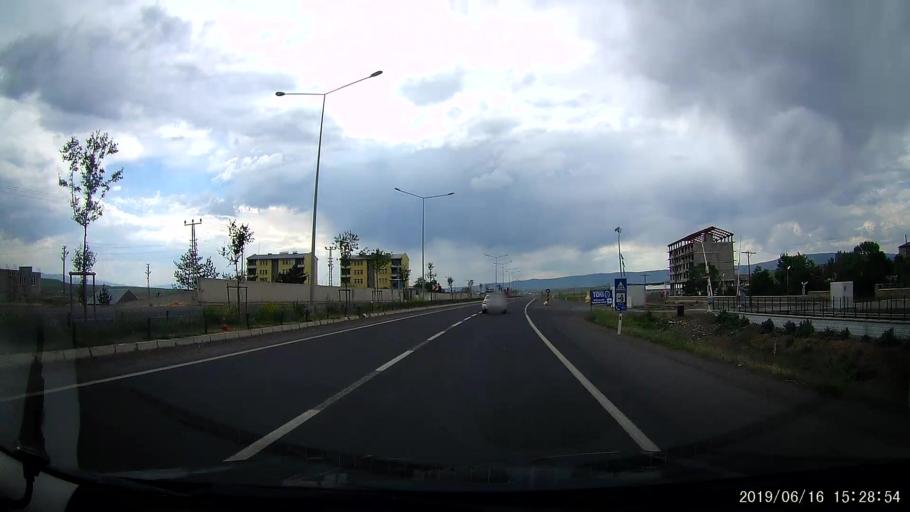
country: TR
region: Erzurum
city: Horasan
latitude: 40.0314
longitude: 42.1436
